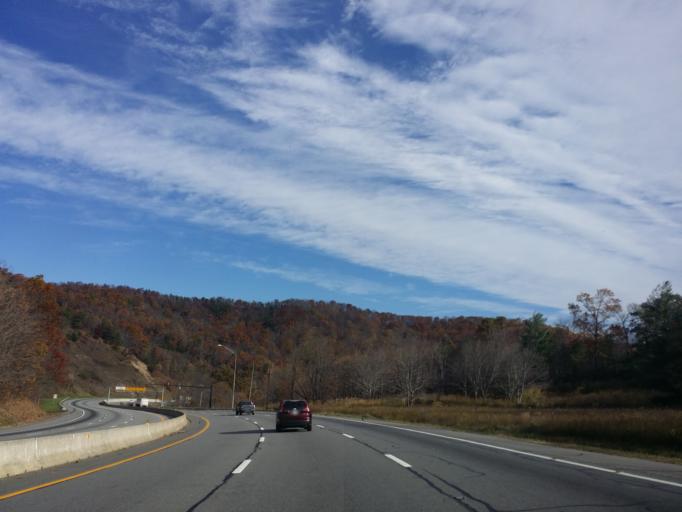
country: US
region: North Carolina
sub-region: Buncombe County
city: Black Mountain
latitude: 35.6195
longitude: -82.2397
